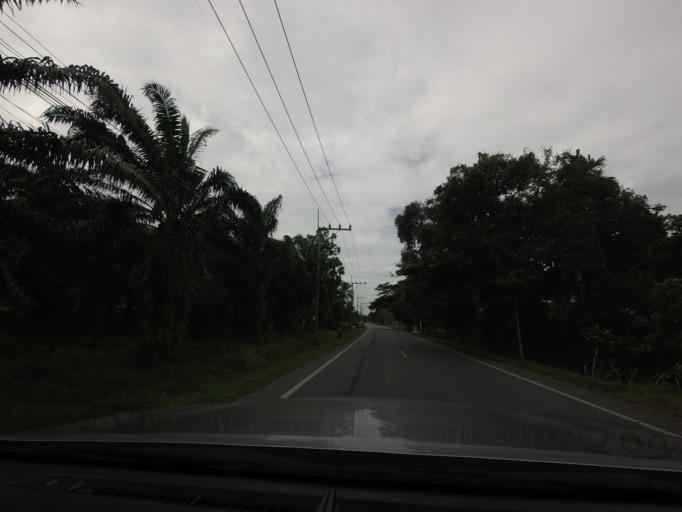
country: TH
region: Nakhon Si Thammarat
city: Phra Phrom
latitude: 8.3077
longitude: 99.9436
